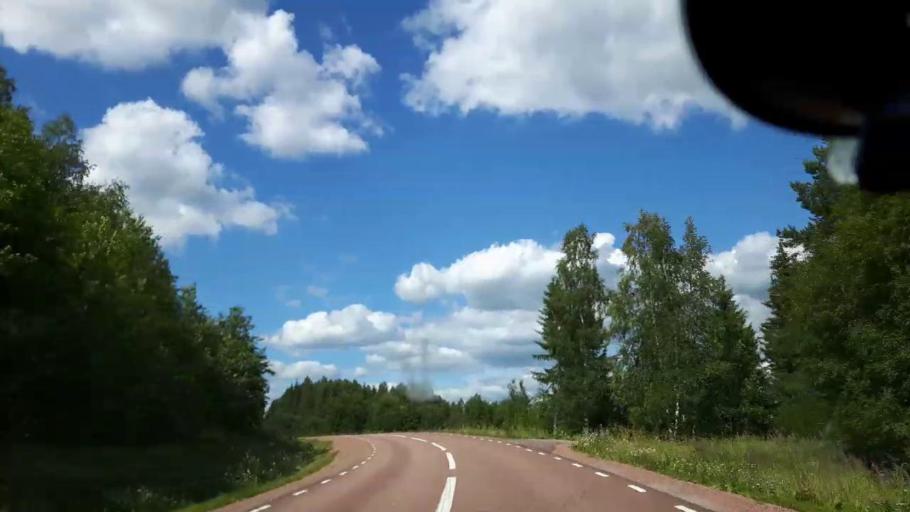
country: SE
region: Jaemtland
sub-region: Ragunda Kommun
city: Hammarstrand
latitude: 63.0237
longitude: 16.5390
